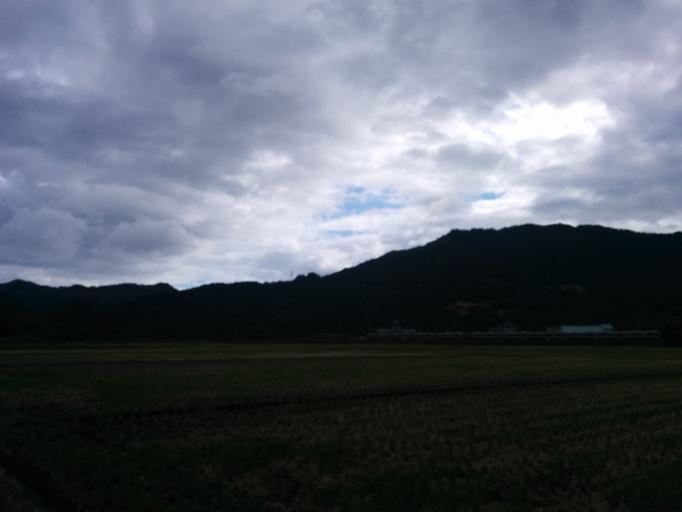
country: JP
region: Shiga Prefecture
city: Omihachiman
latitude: 35.1493
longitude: 136.1382
